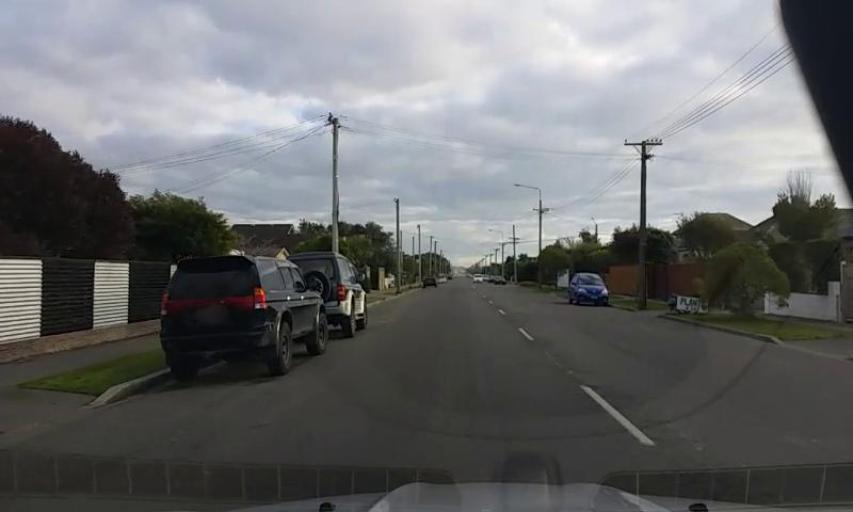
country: NZ
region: Canterbury
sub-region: Christchurch City
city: Christchurch
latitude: -43.5311
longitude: 172.7360
